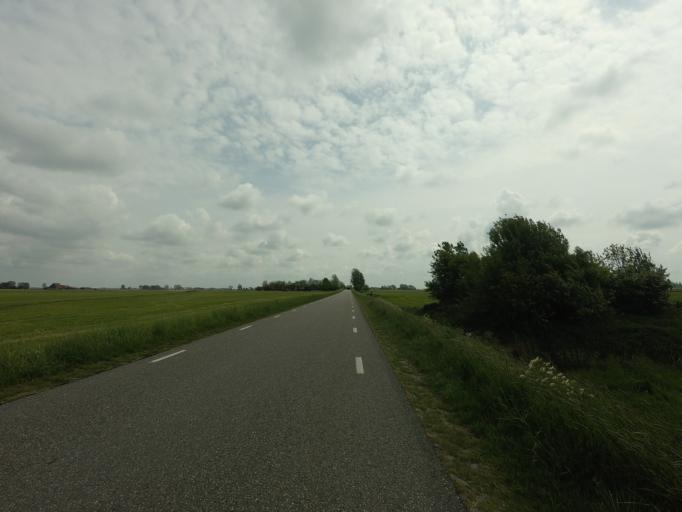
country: NL
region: Friesland
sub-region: Sudwest Fryslan
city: Bolsward
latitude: 53.0974
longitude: 5.5256
